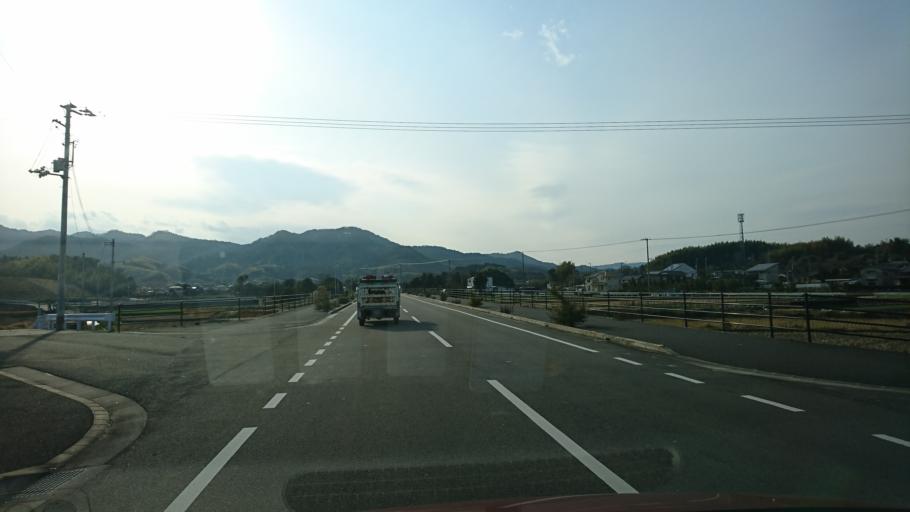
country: JP
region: Ehime
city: Saijo
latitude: 34.0237
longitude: 132.9978
